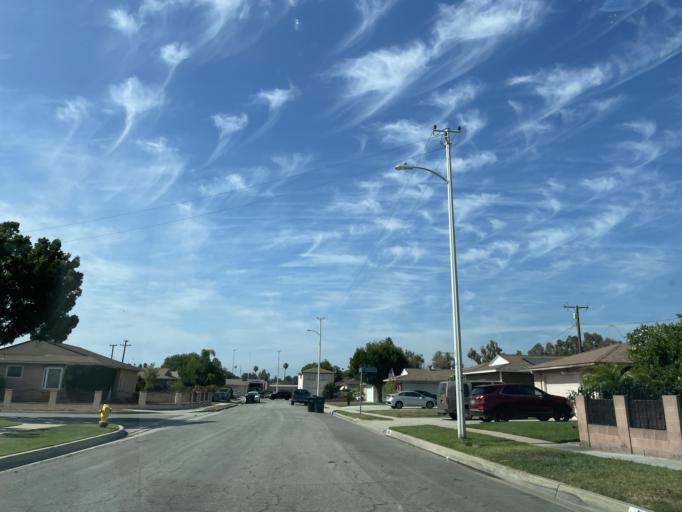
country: US
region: California
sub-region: Los Angeles County
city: Norwalk
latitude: 33.9100
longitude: -118.0613
